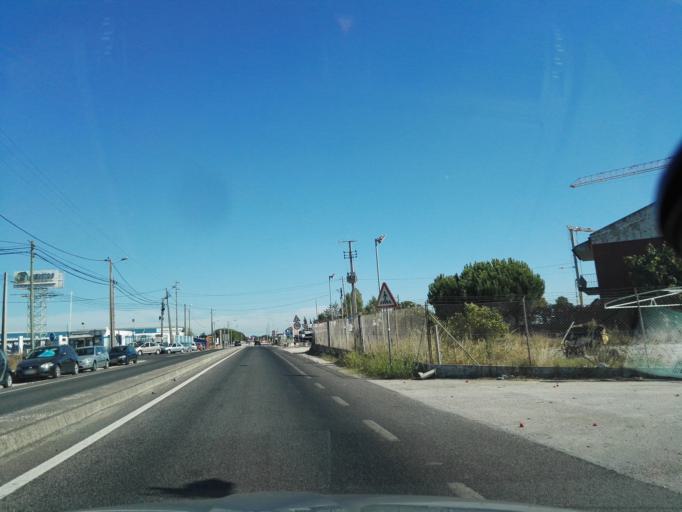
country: PT
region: Santarem
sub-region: Benavente
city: Samora Correia
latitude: 38.9137
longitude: -8.8573
